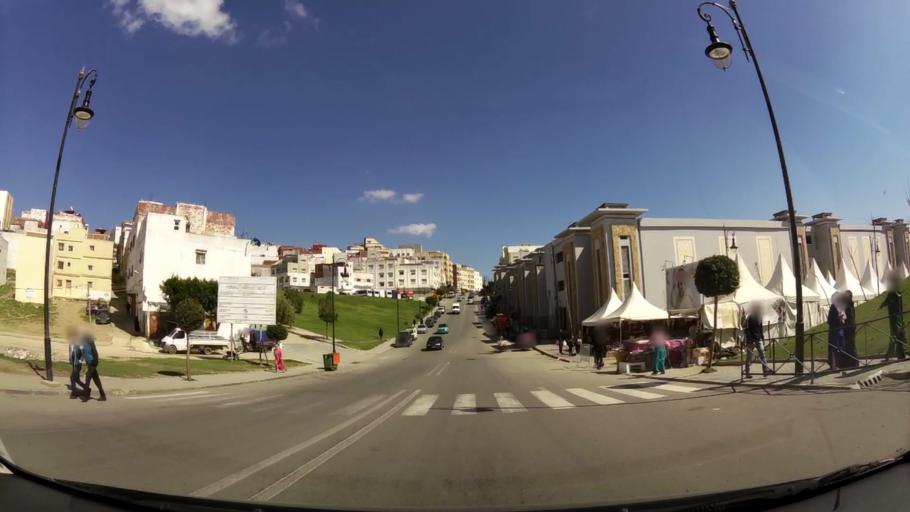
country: MA
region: Tanger-Tetouan
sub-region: Tanger-Assilah
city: Tangier
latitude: 35.7435
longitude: -5.8158
